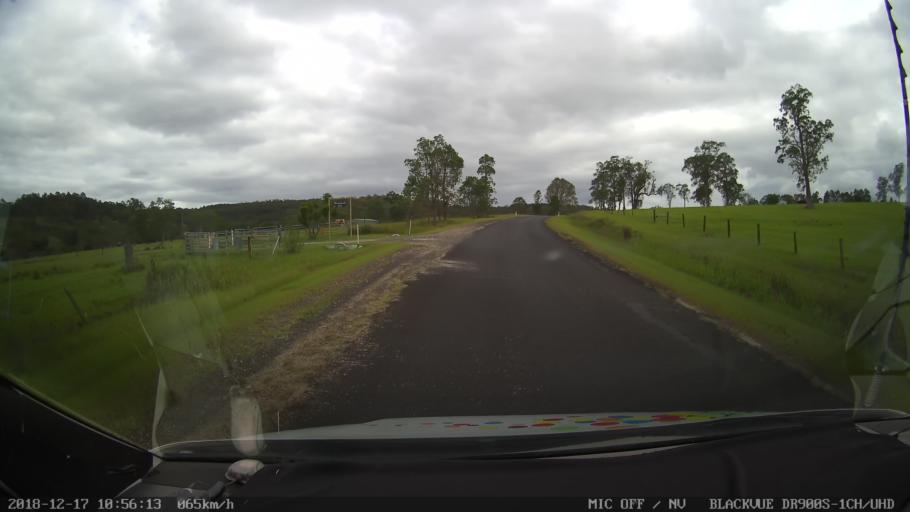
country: AU
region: New South Wales
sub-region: Richmond Valley
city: Casino
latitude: -28.8232
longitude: 152.5860
